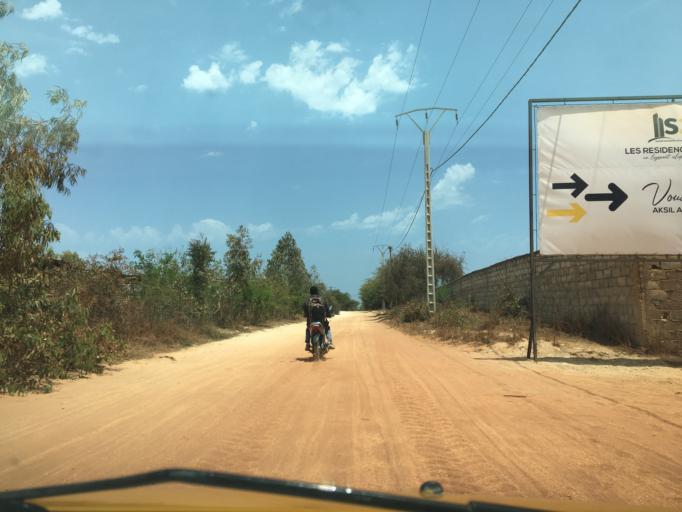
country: SN
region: Thies
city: Thies
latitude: 14.8202
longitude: -17.2008
